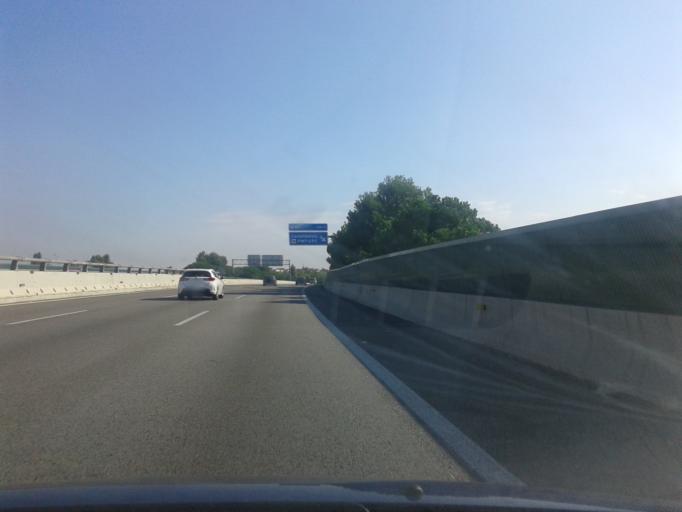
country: ES
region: Catalonia
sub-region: Provincia de Barcelona
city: Castelldefels
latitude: 41.2723
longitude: 1.9713
